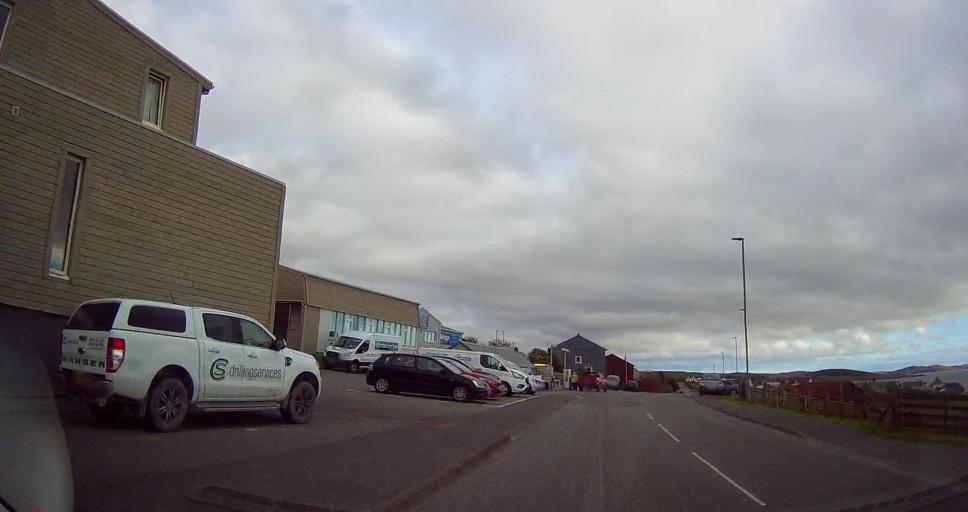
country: GB
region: Scotland
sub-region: Shetland Islands
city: Lerwick
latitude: 60.3922
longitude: -1.3493
